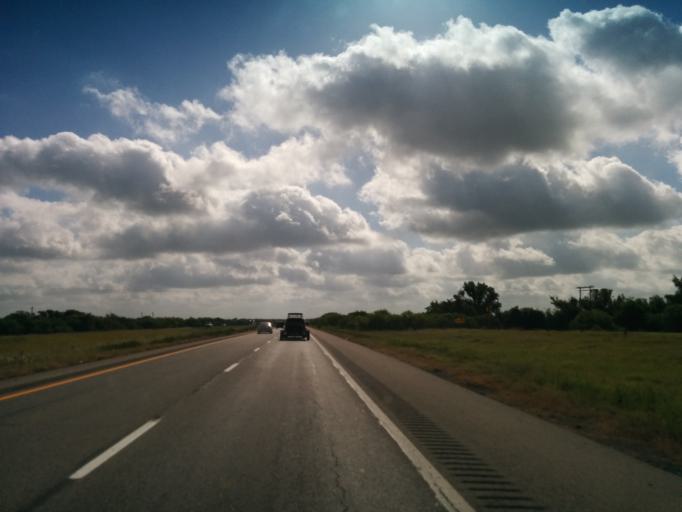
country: US
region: Texas
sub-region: Caldwell County
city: Luling
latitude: 29.6345
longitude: -97.7355
